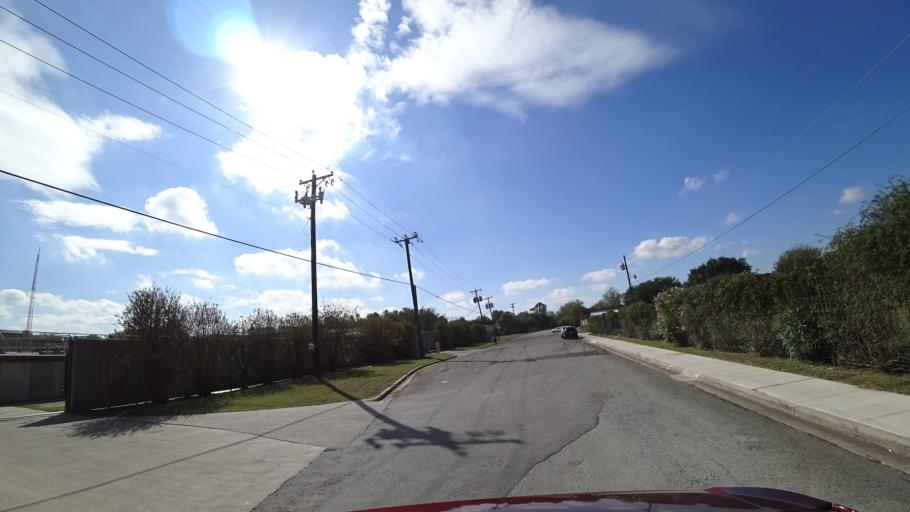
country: US
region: Texas
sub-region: Travis County
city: Windemere
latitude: 30.4564
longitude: -97.6414
